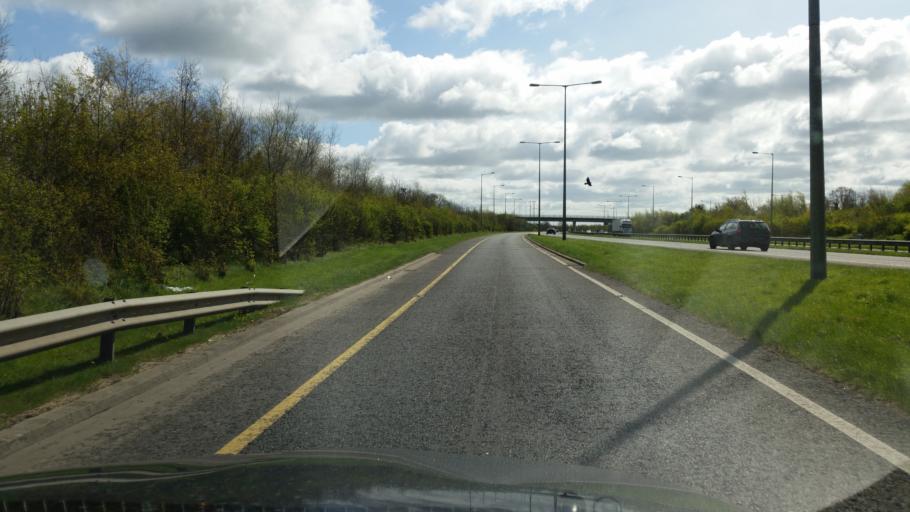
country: IE
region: Leinster
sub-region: An Mhi
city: Ashbourne
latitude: 53.4878
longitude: -6.3848
